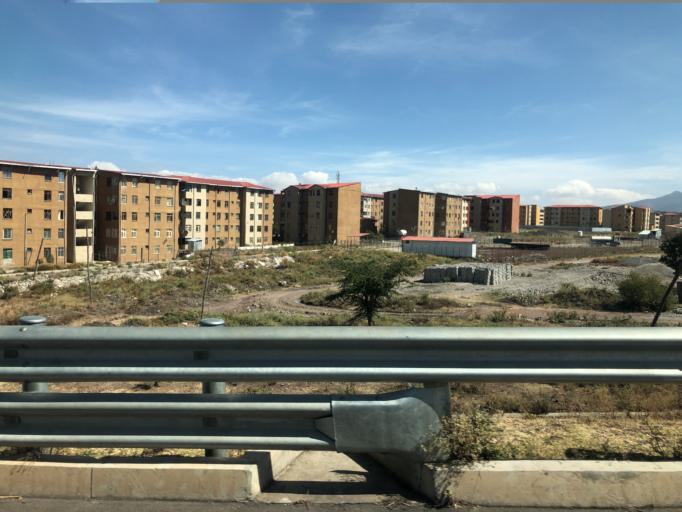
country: ET
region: Adis Abeba
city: Addis Ababa
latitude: 8.8636
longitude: 38.8224
